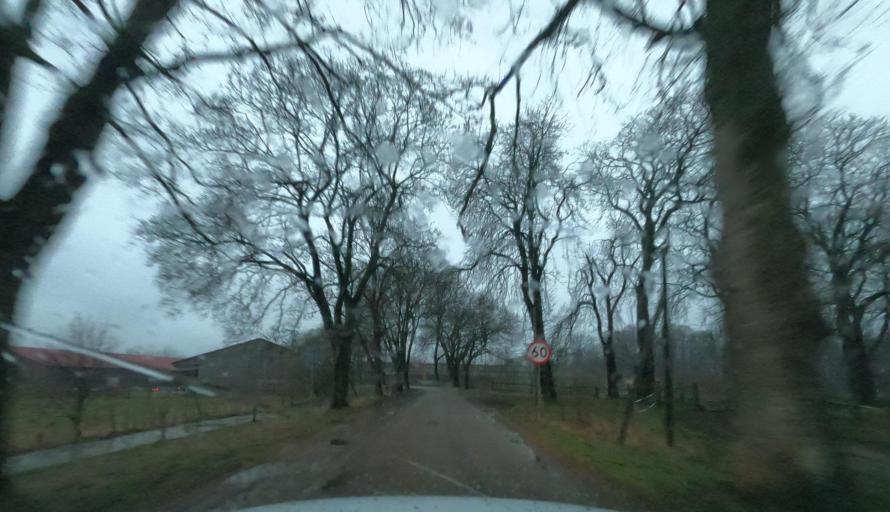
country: PL
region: West Pomeranian Voivodeship
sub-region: Powiat szczecinecki
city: Borne Sulinowo
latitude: 53.6798
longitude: 16.4869
